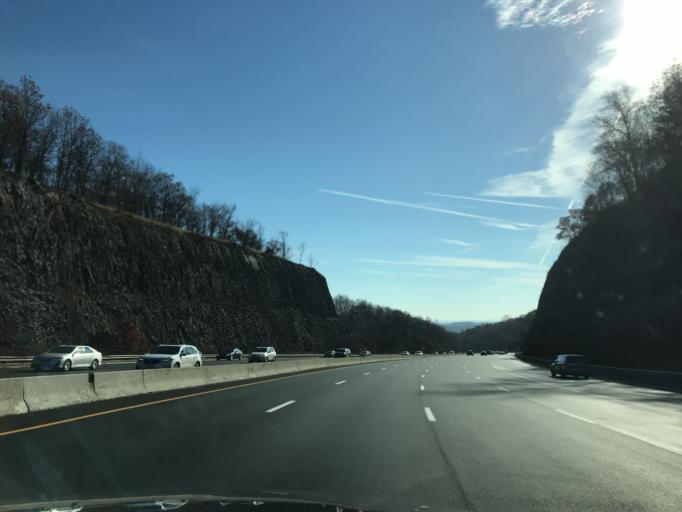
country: US
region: New Jersey
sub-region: Essex County
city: West Orange
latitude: 40.7946
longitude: -74.2491
